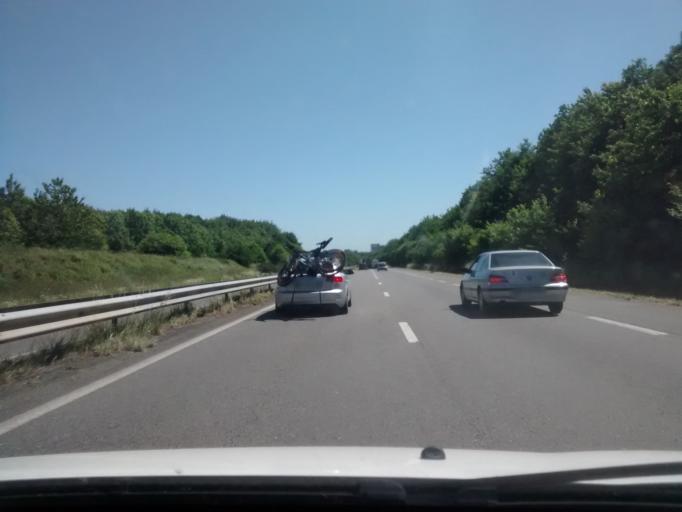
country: FR
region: Brittany
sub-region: Departement d'Ille-et-Vilaine
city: La Meziere
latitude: 48.2094
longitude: -1.7371
